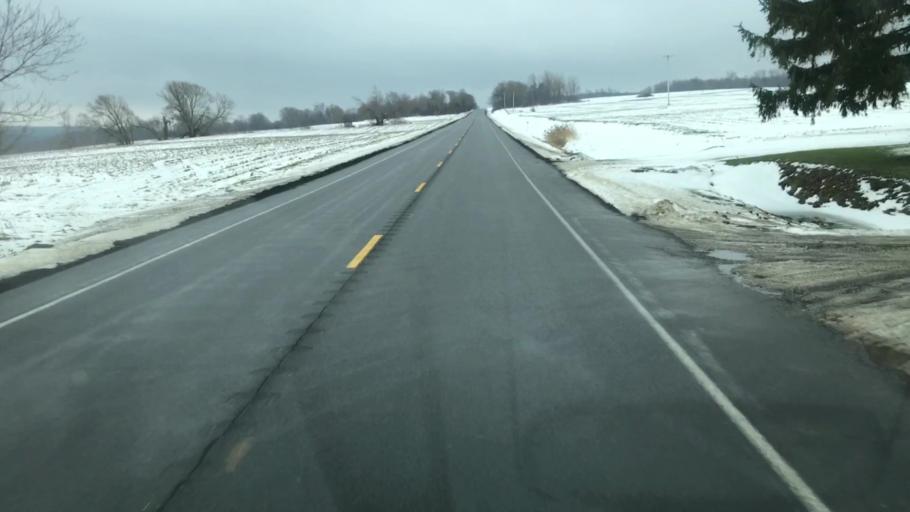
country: US
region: New York
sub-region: Cayuga County
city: Moravia
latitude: 42.7830
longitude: -76.3424
